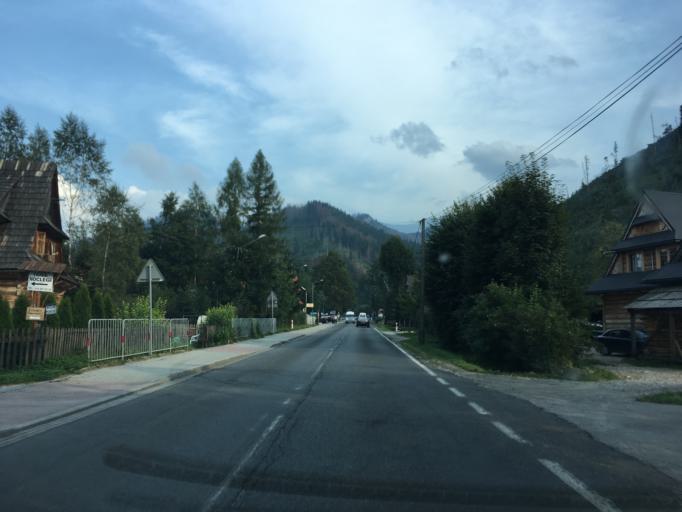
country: PL
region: Lesser Poland Voivodeship
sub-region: Powiat tatrzanski
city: Koscielisko
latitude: 49.2781
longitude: 19.8645
